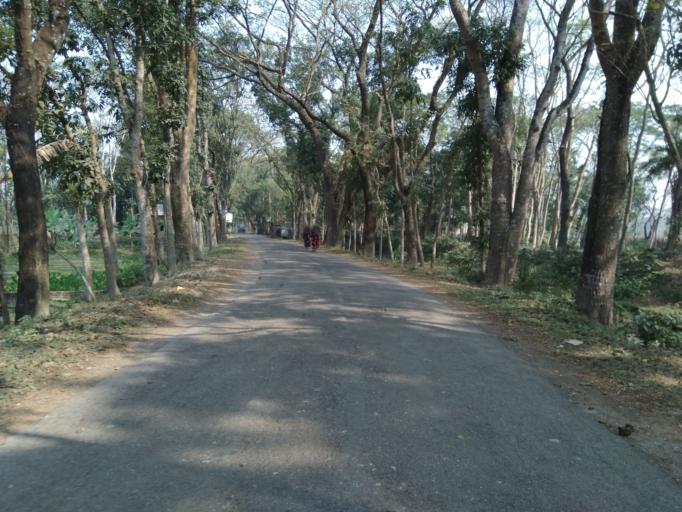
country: BD
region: Barisal
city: Mehendiganj
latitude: 22.9583
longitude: 90.4150
